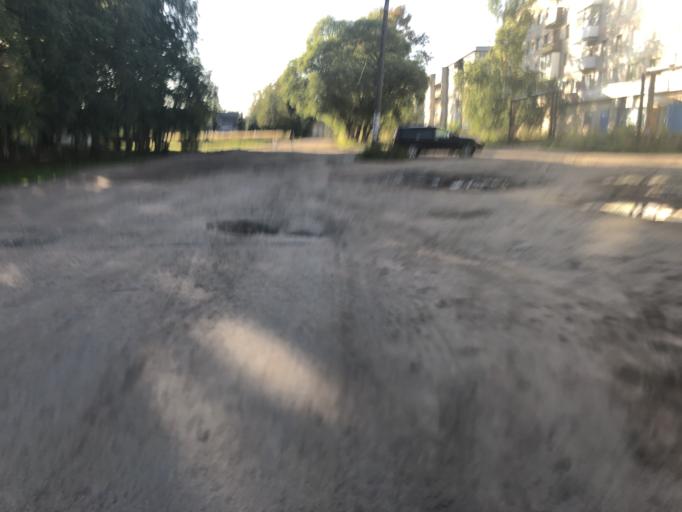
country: RU
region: Tverskaya
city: Rzhev
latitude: 56.2433
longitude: 34.3138
